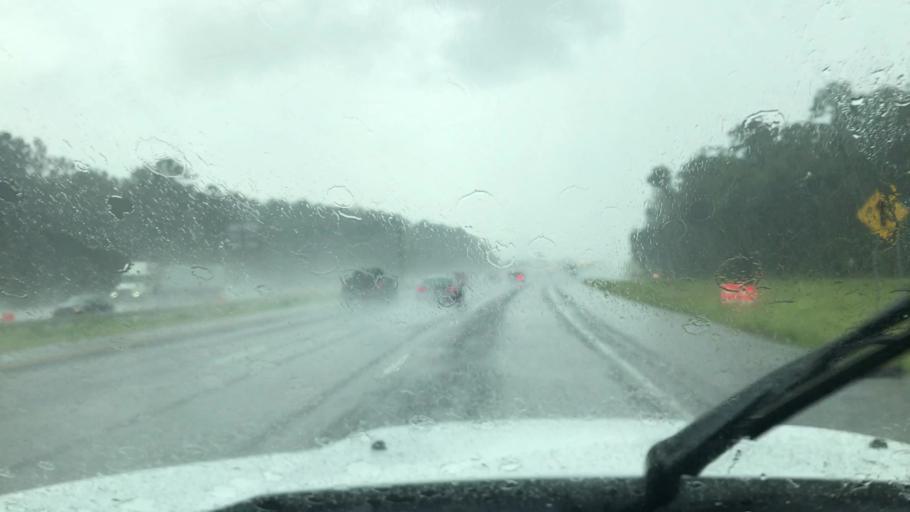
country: US
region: Georgia
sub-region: Camden County
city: Woodbine
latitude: 30.9483
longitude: -81.6857
